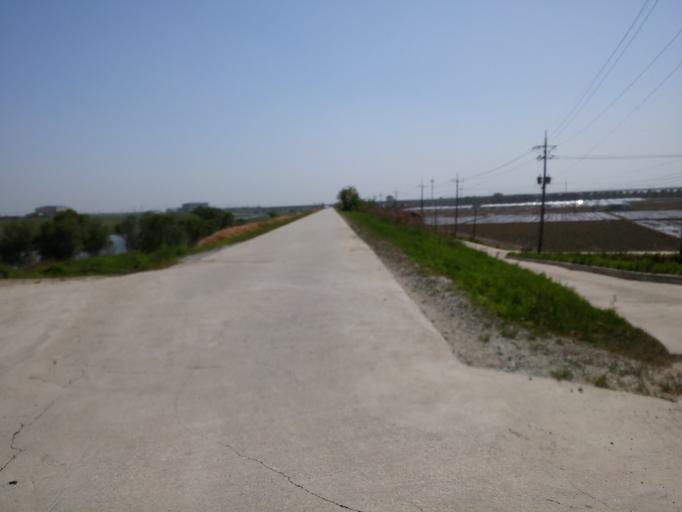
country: KR
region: Chungcheongnam-do
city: Nonsan
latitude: 36.1913
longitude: 127.0584
